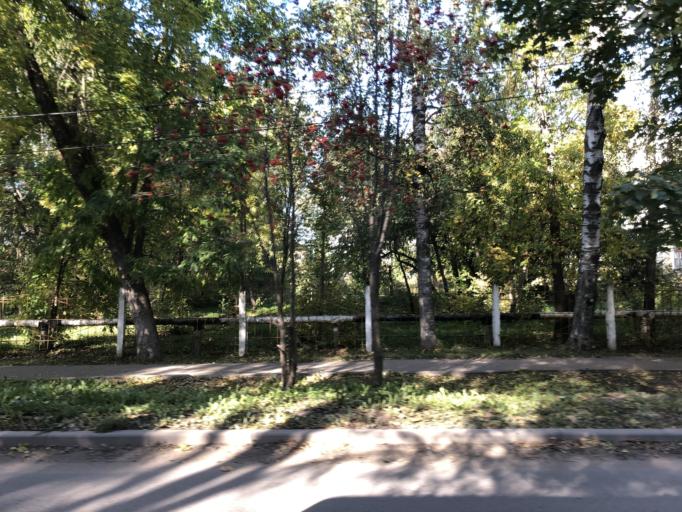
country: RU
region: Tverskaya
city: Rzhev
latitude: 56.2618
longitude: 34.3517
